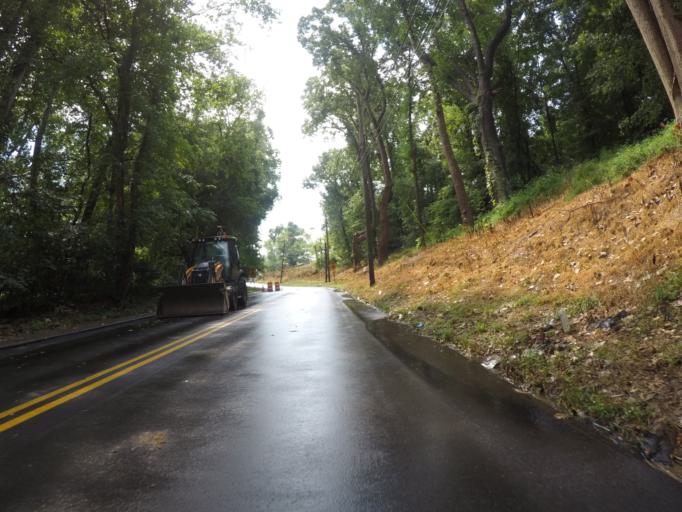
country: US
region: Kentucky
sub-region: Boyd County
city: Westwood
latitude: 38.4763
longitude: -82.6652
